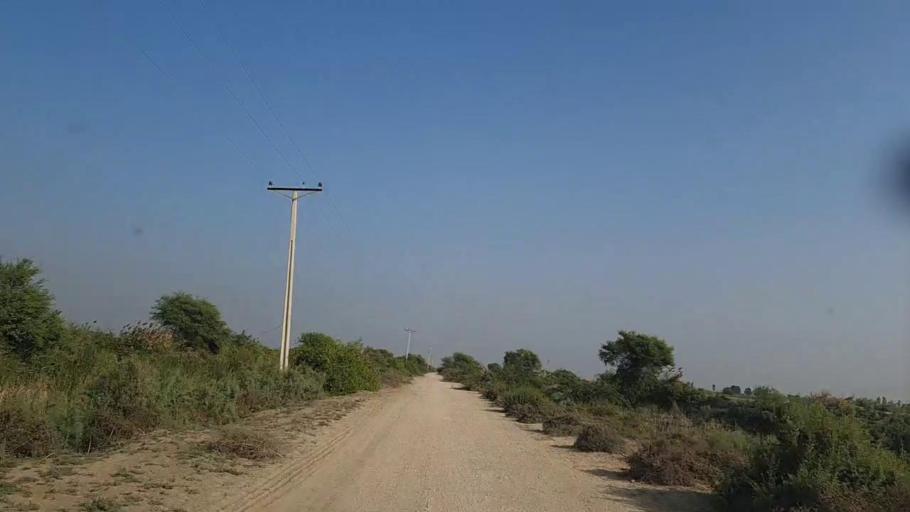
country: PK
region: Sindh
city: Jati
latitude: 24.4602
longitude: 68.3030
